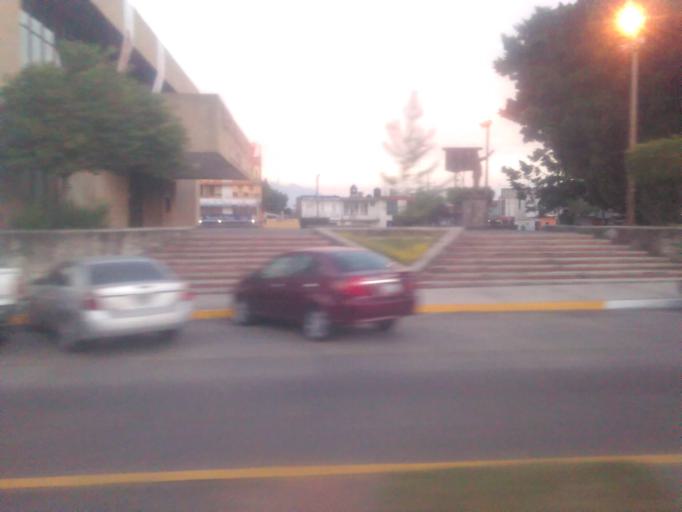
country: MX
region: Nayarit
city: Tepic
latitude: 21.5147
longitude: -104.8990
